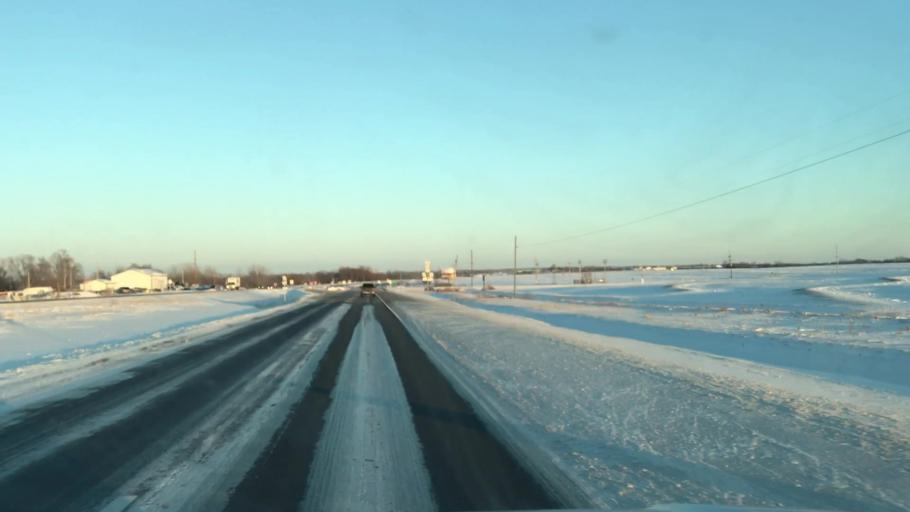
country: US
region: Missouri
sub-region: Clinton County
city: Cameron
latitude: 39.7615
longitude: -94.3611
